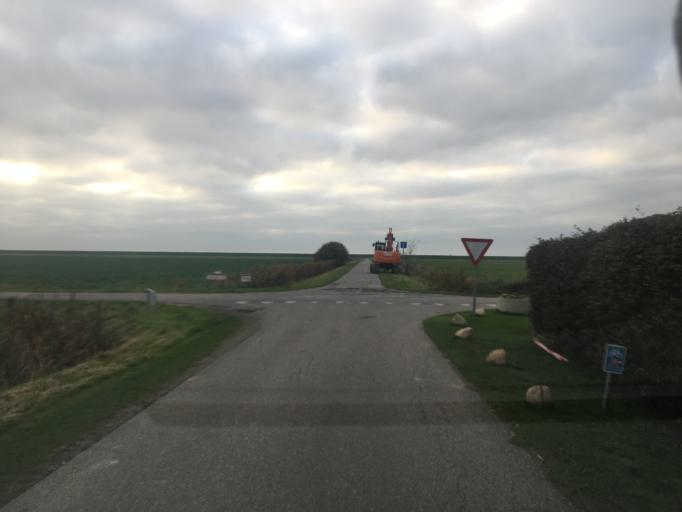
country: DE
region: Schleswig-Holstein
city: Klanxbull
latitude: 54.9261
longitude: 8.6794
